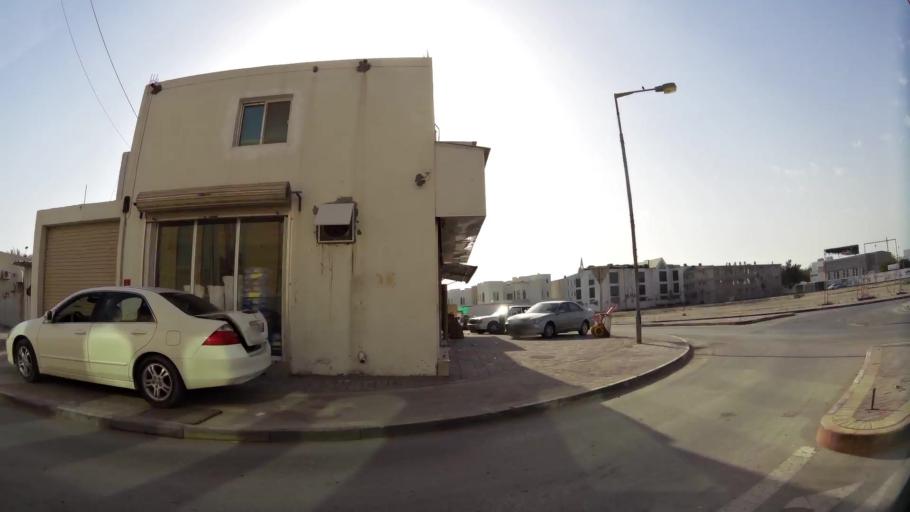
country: BH
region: Manama
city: Jidd Hafs
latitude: 26.2138
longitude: 50.5127
